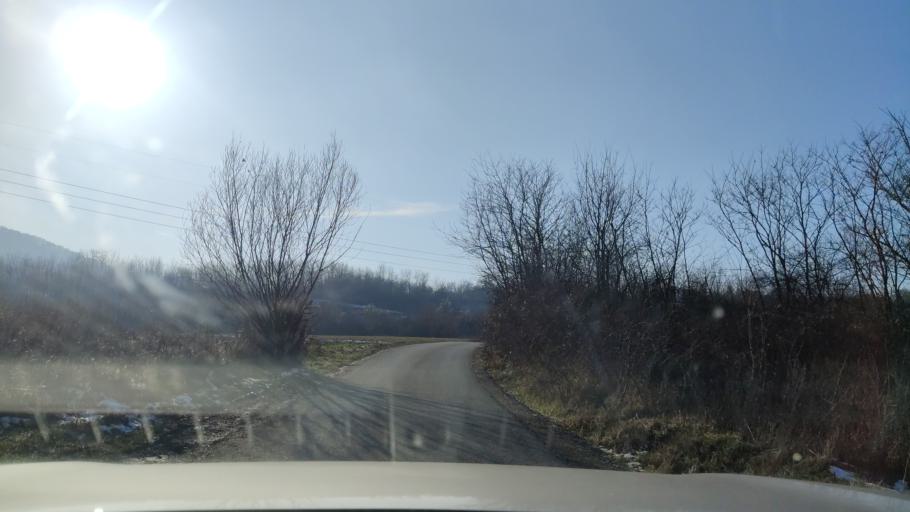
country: RS
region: Central Serbia
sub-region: Belgrade
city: Zvezdara
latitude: 44.7119
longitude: 20.5123
